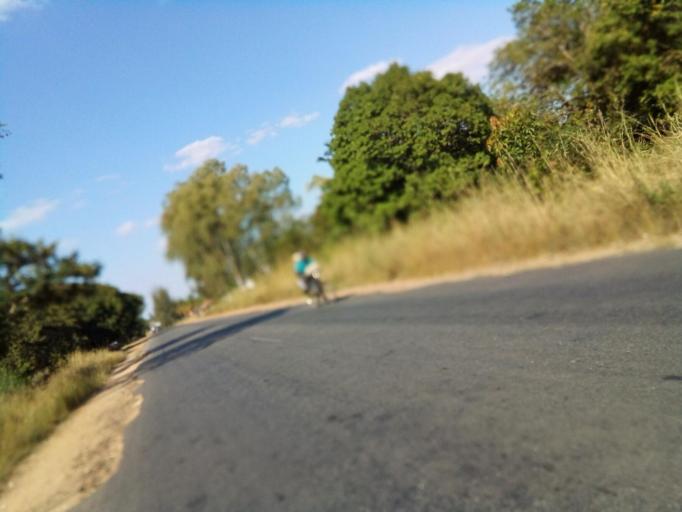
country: MZ
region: Zambezia
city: Quelimane
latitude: -17.5760
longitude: 36.6394
